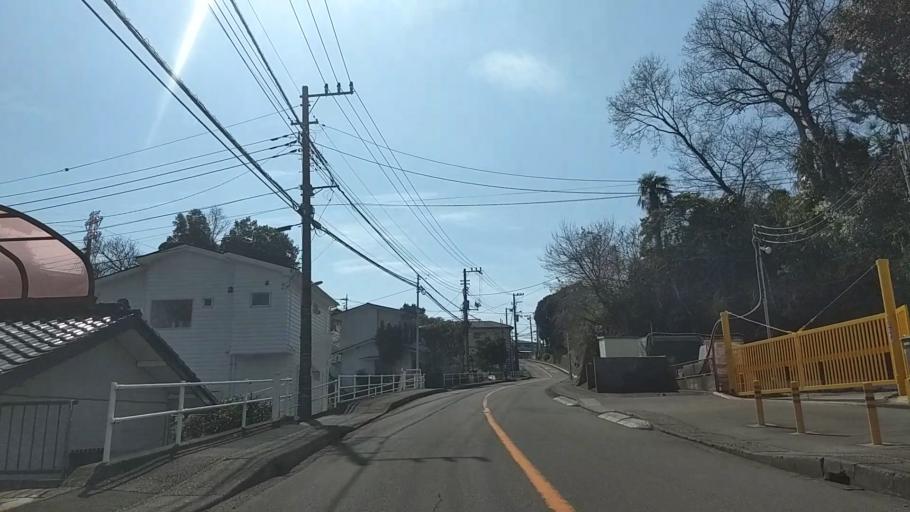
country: JP
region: Kanagawa
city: Chigasaki
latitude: 35.3719
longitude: 139.4259
